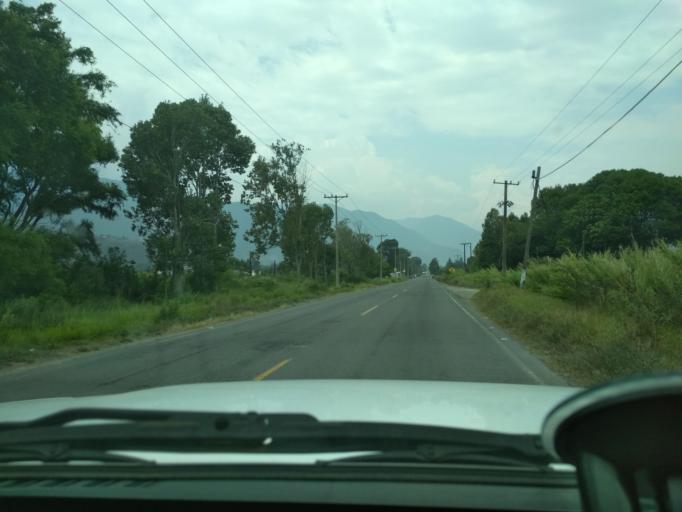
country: MX
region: Veracruz
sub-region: Nogales
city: Taza de Agua Ojo Zarco
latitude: 18.7744
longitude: -97.2132
